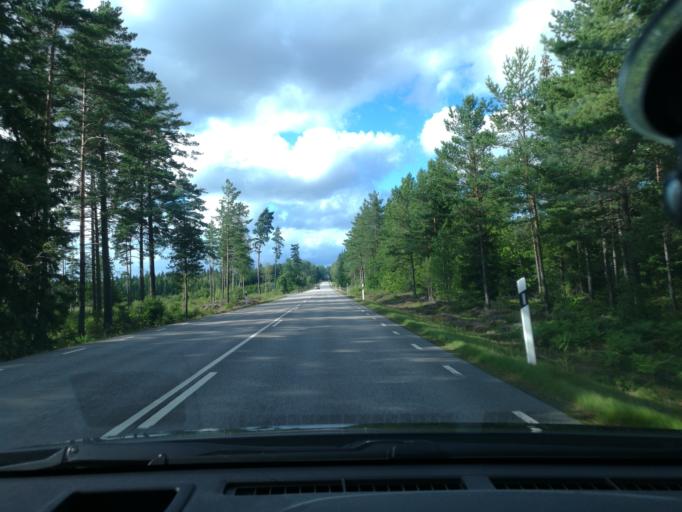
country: SE
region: Kronoberg
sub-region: Vaxjo Kommun
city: Braas
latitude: 57.0416
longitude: 15.0649
